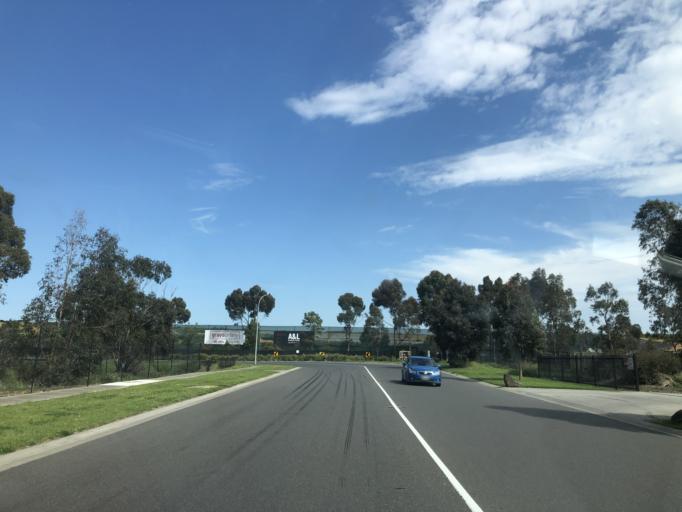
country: AU
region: Victoria
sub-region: Casey
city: Hampton Park
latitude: -38.0400
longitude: 145.2335
